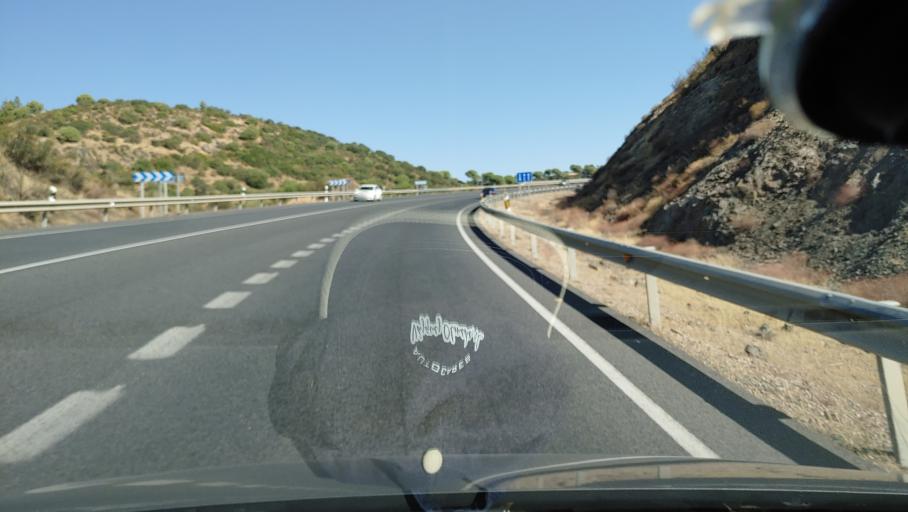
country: ES
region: Andalusia
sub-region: Province of Cordoba
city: Cordoba
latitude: 37.9831
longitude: -4.7871
